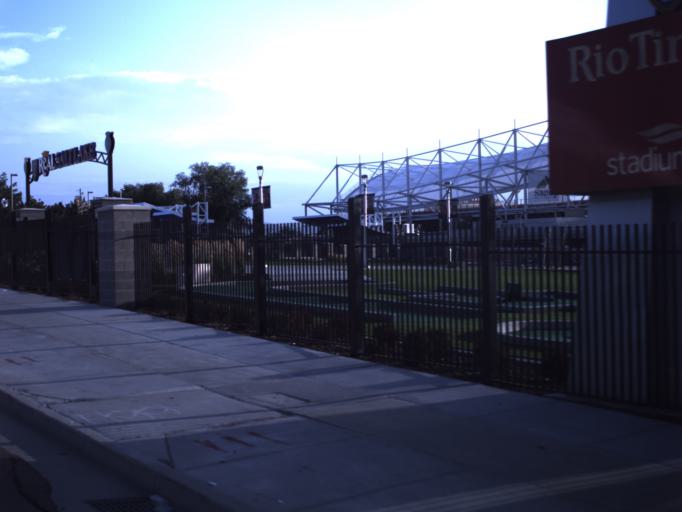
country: US
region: Utah
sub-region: Salt Lake County
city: Sandy City
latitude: 40.5839
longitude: -111.8910
